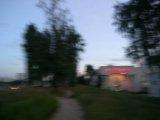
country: RU
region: Moscow
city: Strogino
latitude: 55.8171
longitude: 37.3901
